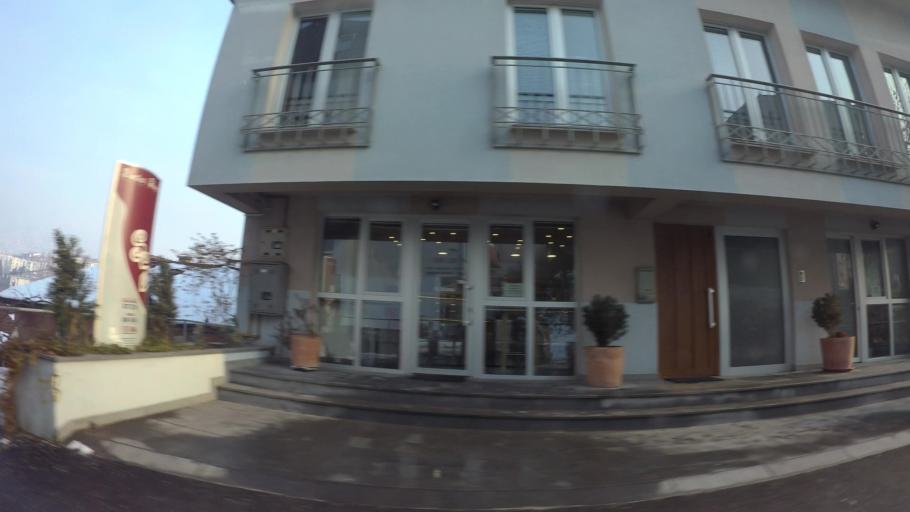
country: BA
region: Federation of Bosnia and Herzegovina
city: Kobilja Glava
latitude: 43.8673
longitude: 18.4006
